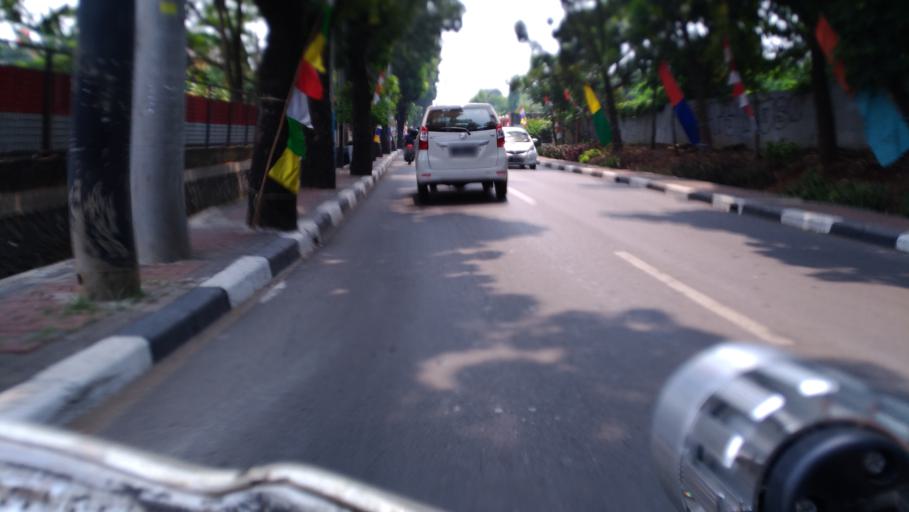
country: ID
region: West Java
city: Cileungsir
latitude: -6.3182
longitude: 106.8906
